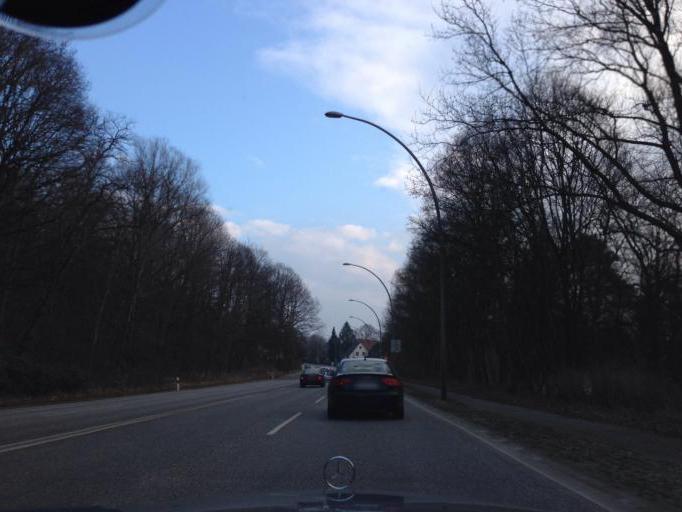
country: DE
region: Hamburg
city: Bergedorf
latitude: 53.4971
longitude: 10.1902
